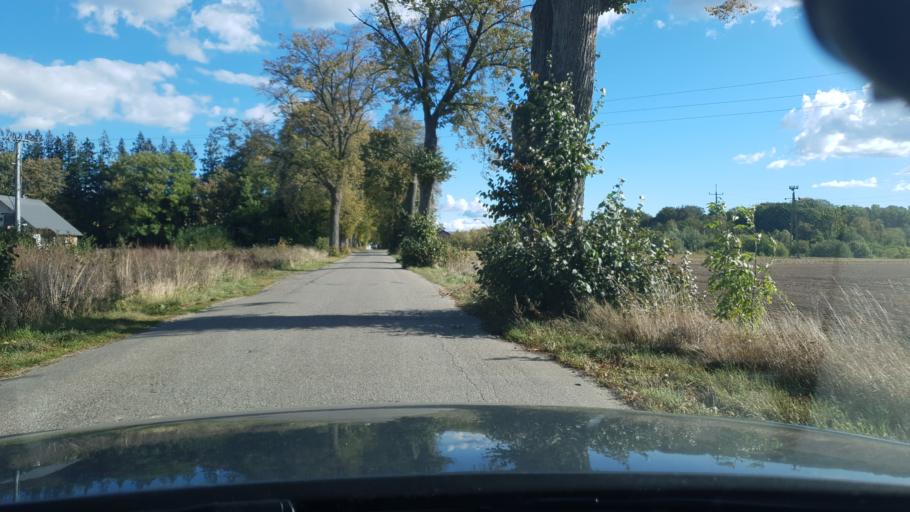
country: PL
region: Pomeranian Voivodeship
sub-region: Powiat pucki
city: Zelistrzewo
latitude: 54.6863
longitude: 18.4575
